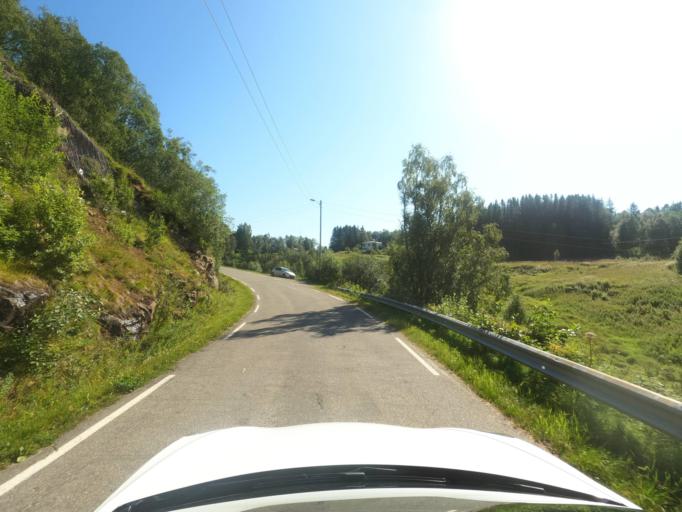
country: NO
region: Nordland
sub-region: Hadsel
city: Stokmarknes
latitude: 68.3045
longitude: 15.0702
